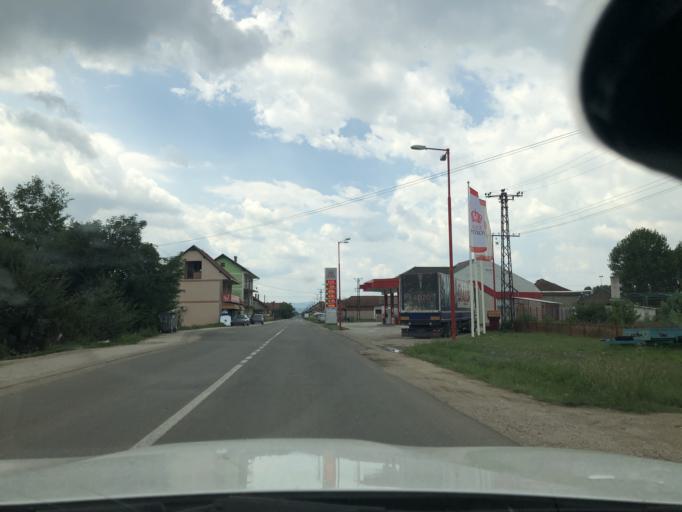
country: RS
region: Central Serbia
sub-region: Jablanicki Okrug
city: Lebane
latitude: 42.9623
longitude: 21.8374
